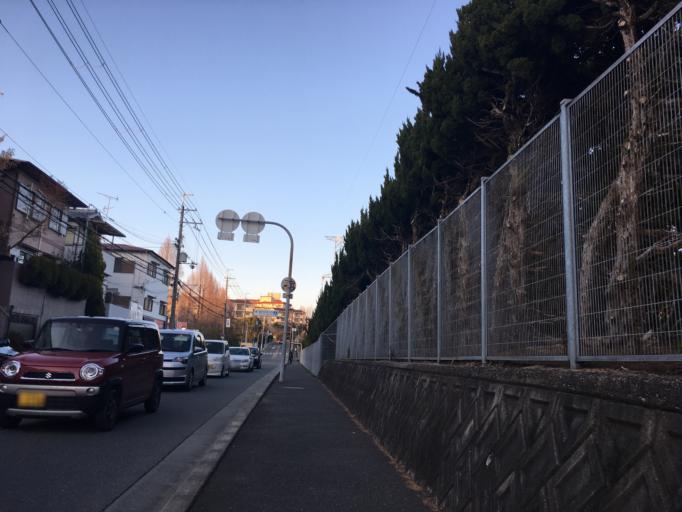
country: JP
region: Osaka
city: Mino
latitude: 34.8386
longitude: 135.5150
